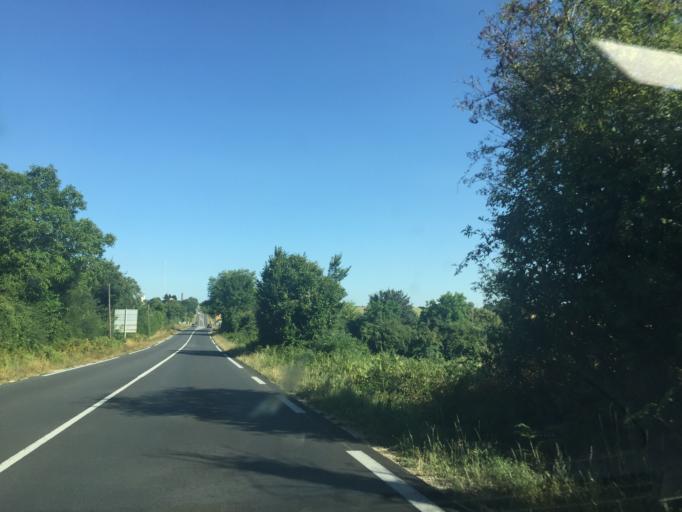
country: FR
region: Poitou-Charentes
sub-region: Departement des Deux-Sevres
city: Melle
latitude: 46.2079
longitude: -0.1051
